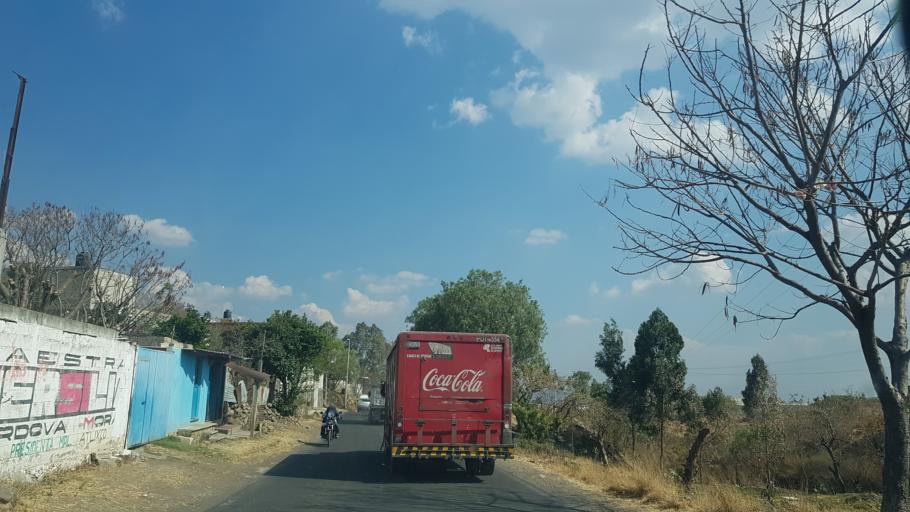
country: MX
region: Puebla
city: Atlixco
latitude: 18.9134
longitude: -98.4786
